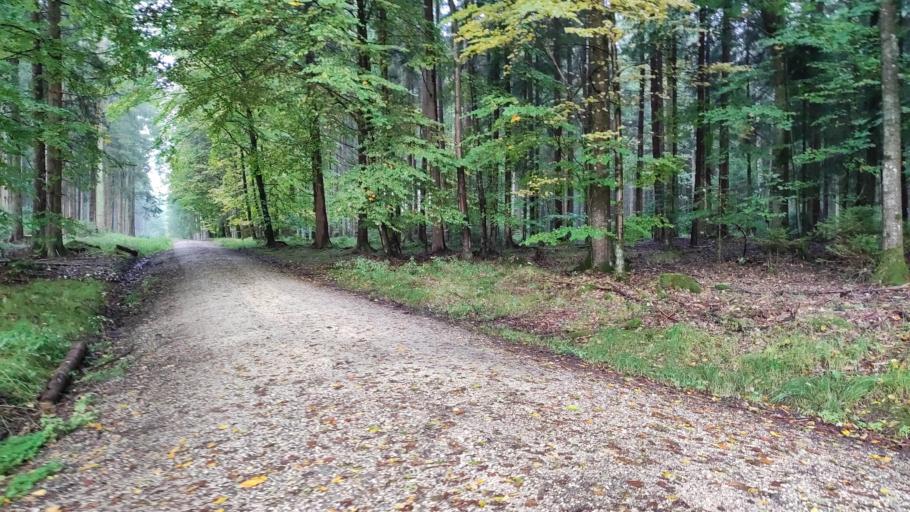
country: DE
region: Bavaria
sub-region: Swabia
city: Welden
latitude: 48.4296
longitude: 10.6404
